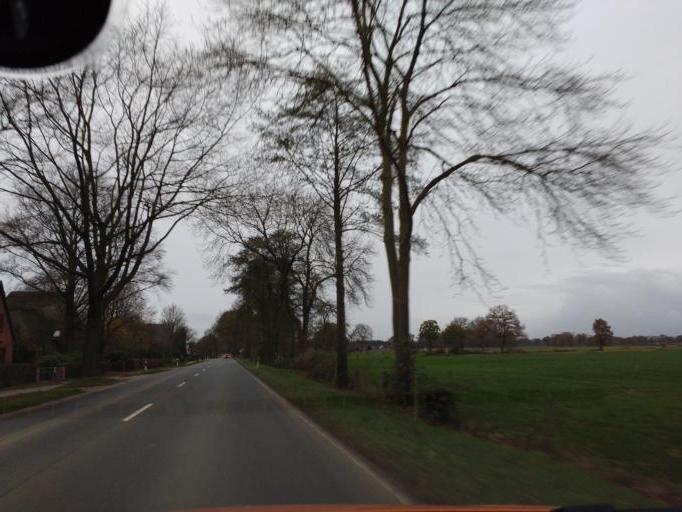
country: DE
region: Lower Saxony
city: Hude
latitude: 53.0656
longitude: 8.4349
